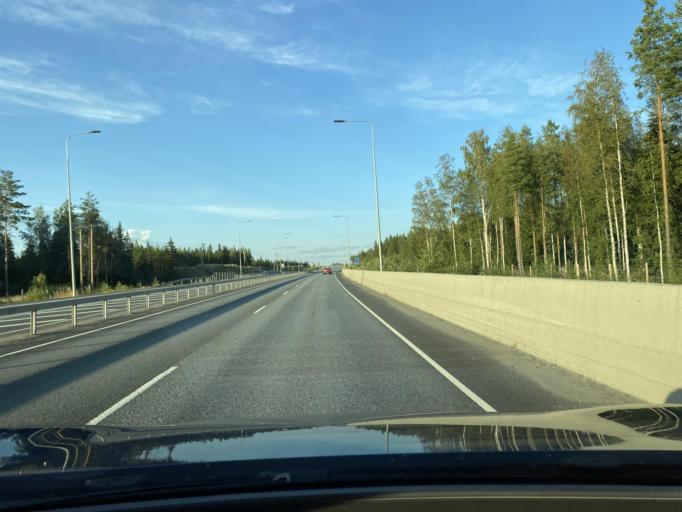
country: FI
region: Southern Ostrobothnia
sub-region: Seinaejoki
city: Seinaejoki
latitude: 62.7331
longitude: 22.8981
